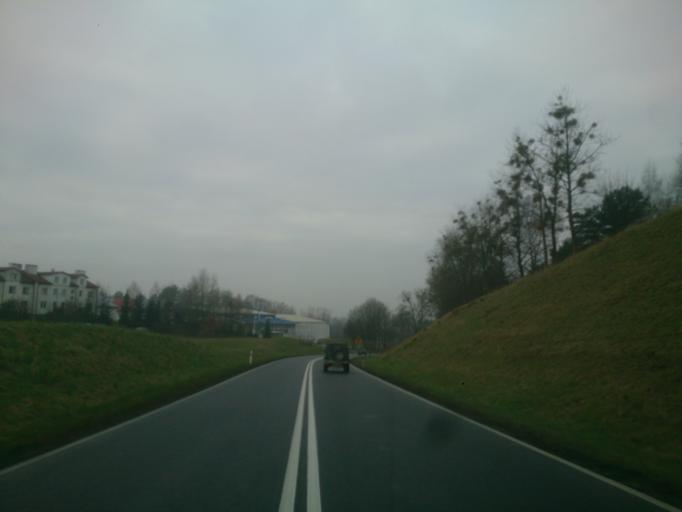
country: PL
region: Pomeranian Voivodeship
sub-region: Powiat bytowski
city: Miastko
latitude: 54.0075
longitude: 17.0079
